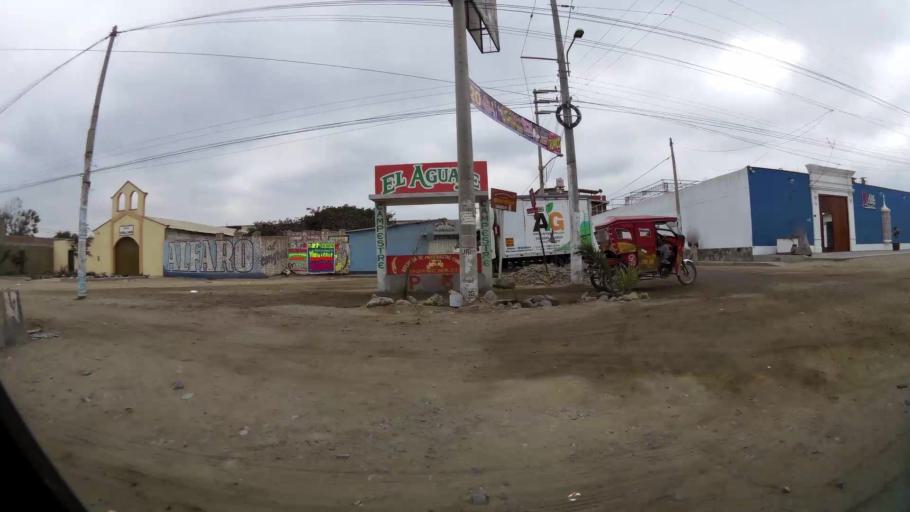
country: PE
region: La Libertad
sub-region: Provincia de Trujillo
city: Huanchaco
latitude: -8.0894
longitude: -79.0898
